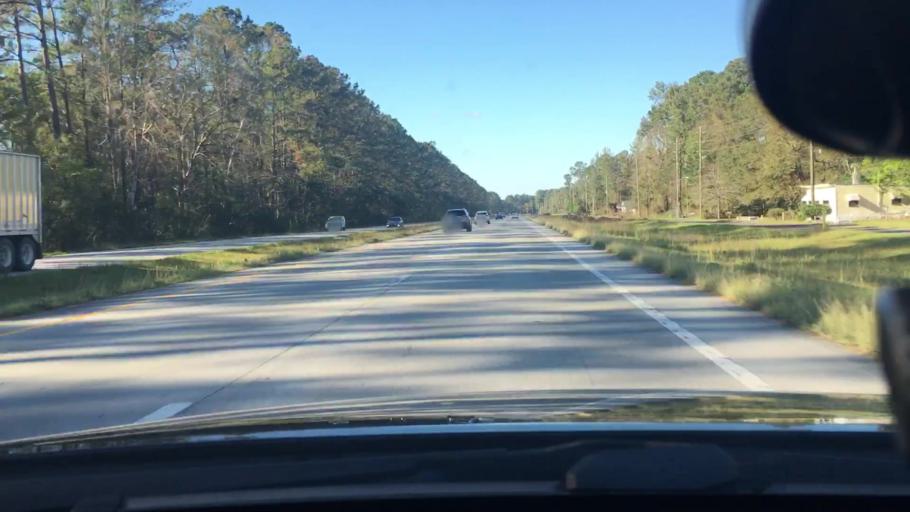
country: US
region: North Carolina
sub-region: Craven County
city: Neuse Forest
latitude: 34.9801
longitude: -76.9771
